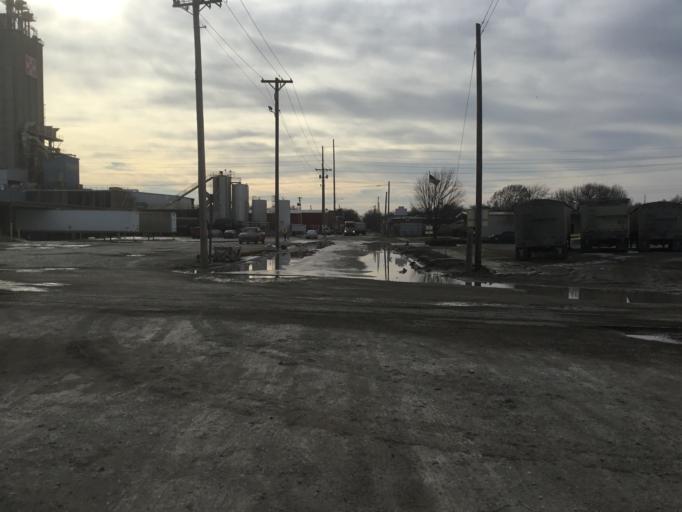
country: US
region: Kansas
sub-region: Sedgwick County
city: Wichita
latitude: 37.7172
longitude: -97.3324
